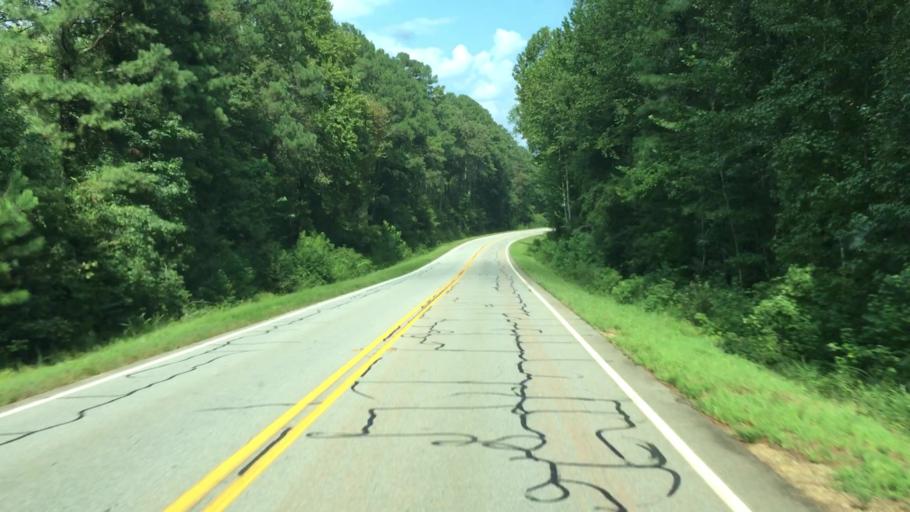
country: US
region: Georgia
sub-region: Butts County
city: Indian Springs
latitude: 33.1734
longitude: -83.8061
